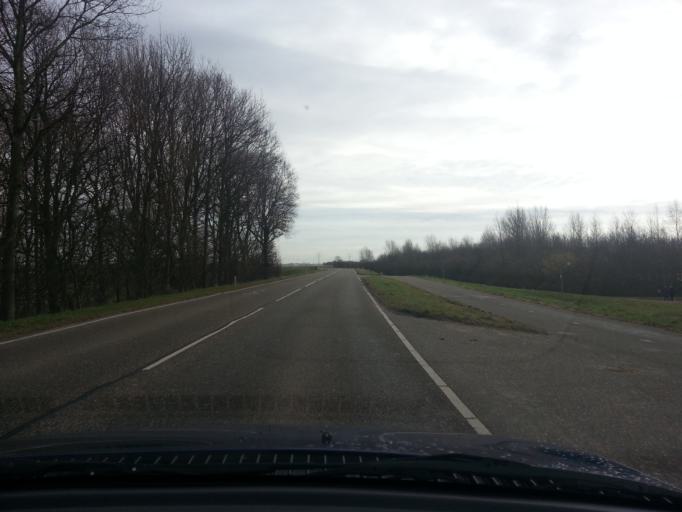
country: NL
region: South Holland
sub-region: Gemeente Spijkenisse
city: Spijkenisse
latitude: 51.8271
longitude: 4.2731
